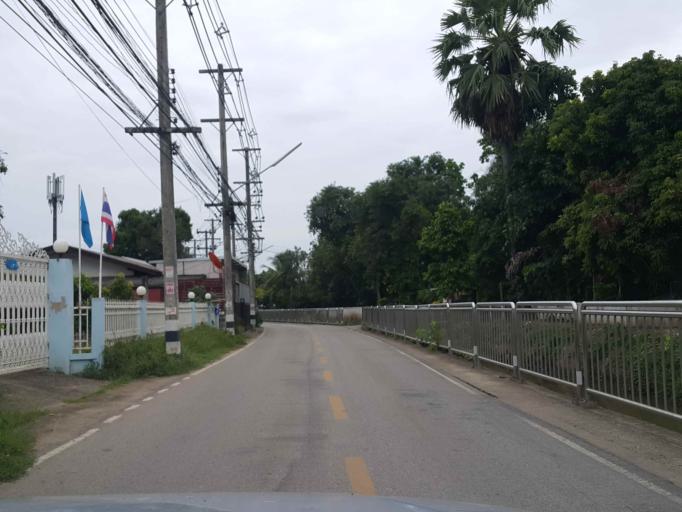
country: TH
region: Chiang Mai
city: Chiang Mai
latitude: 18.7643
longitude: 99.0131
